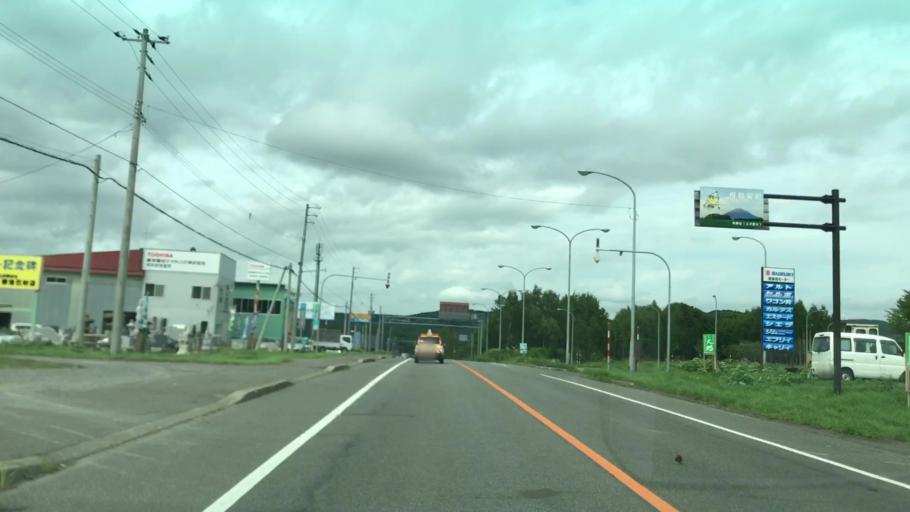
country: JP
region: Hokkaido
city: Niseko Town
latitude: 42.9144
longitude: 140.7505
